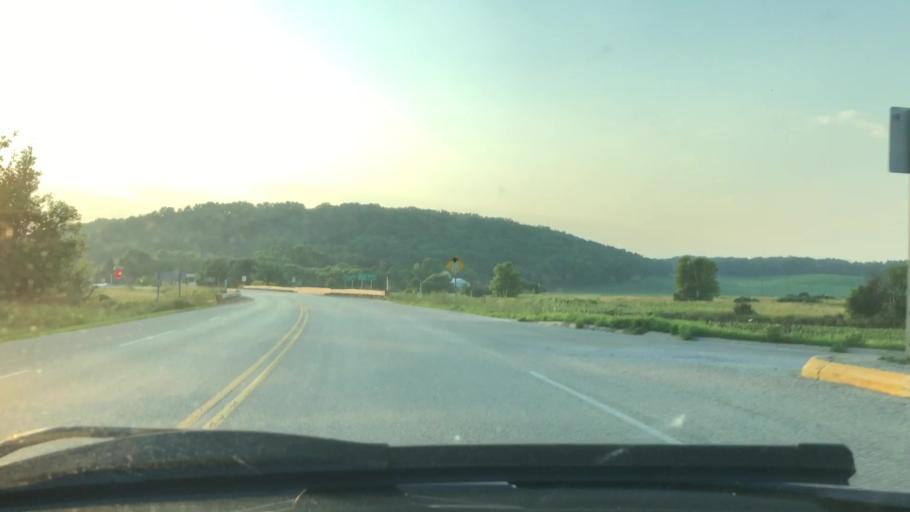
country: US
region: Wisconsin
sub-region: Dane County
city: Black Earth
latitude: 43.1409
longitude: -89.7423
